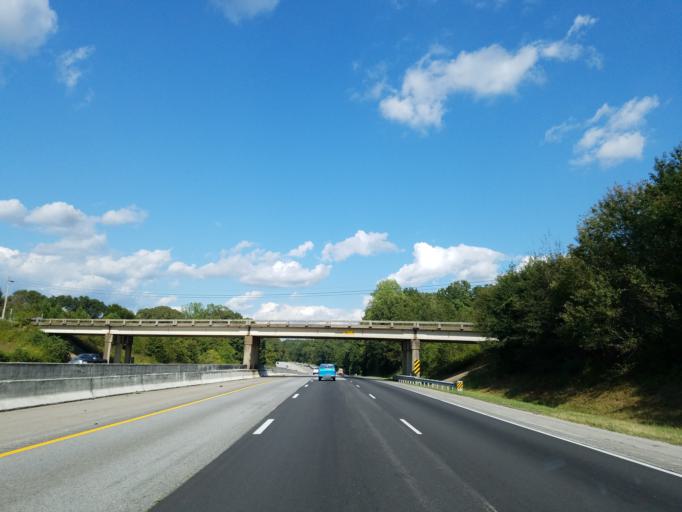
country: US
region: South Carolina
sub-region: Anderson County
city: Northlake
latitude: 34.6065
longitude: -82.6364
